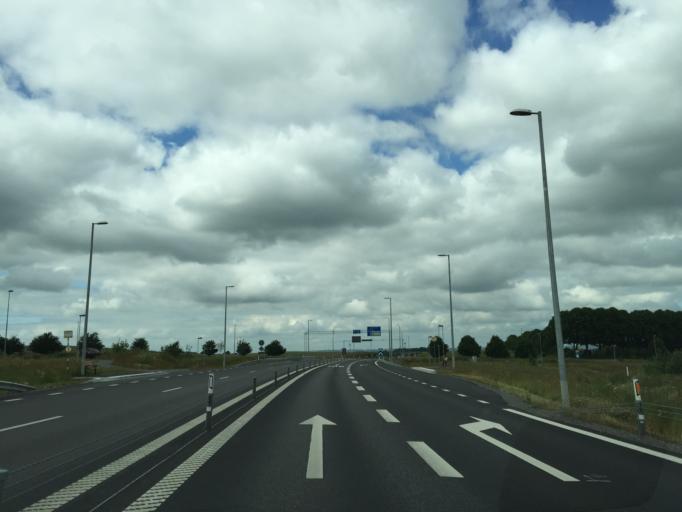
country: SE
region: Skane
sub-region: Svedala Kommun
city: Klagerup
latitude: 55.5776
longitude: 13.2527
